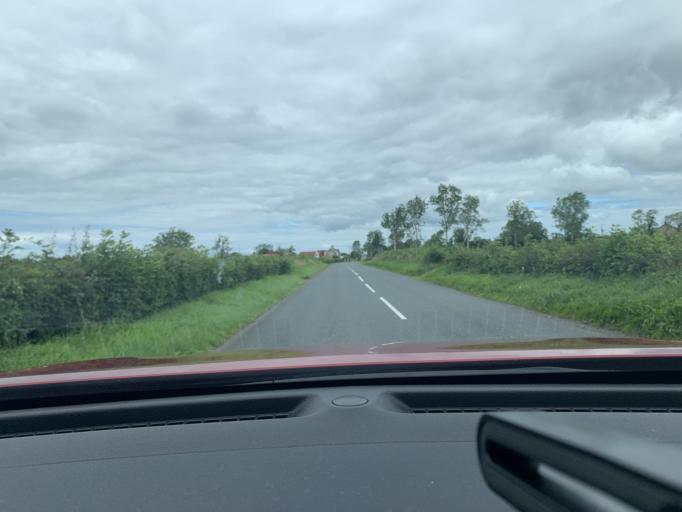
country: GB
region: Northern Ireland
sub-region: Fermanagh District
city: Enniskillen
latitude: 54.2767
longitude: -7.7030
